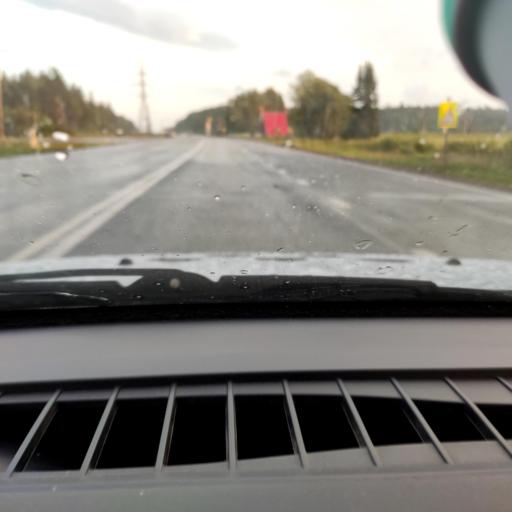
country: RU
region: Udmurtiya
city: Balezino
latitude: 57.9616
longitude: 52.9709
